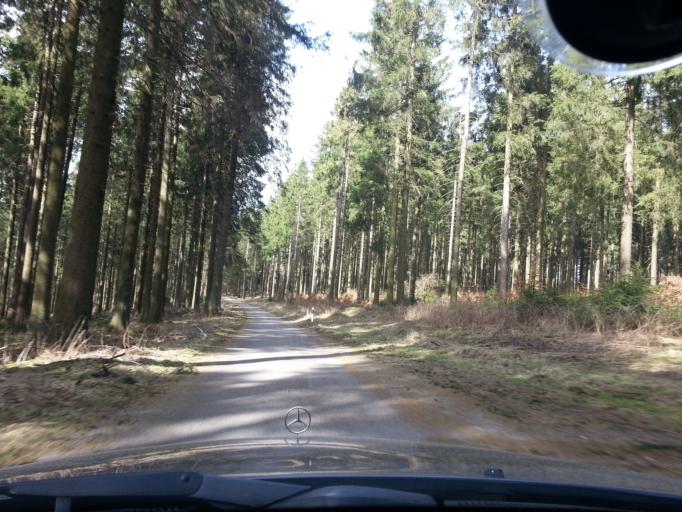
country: DE
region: North Rhine-Westphalia
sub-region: Regierungsbezirk Arnsberg
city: Bad Fredeburg
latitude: 51.2089
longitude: 8.3546
